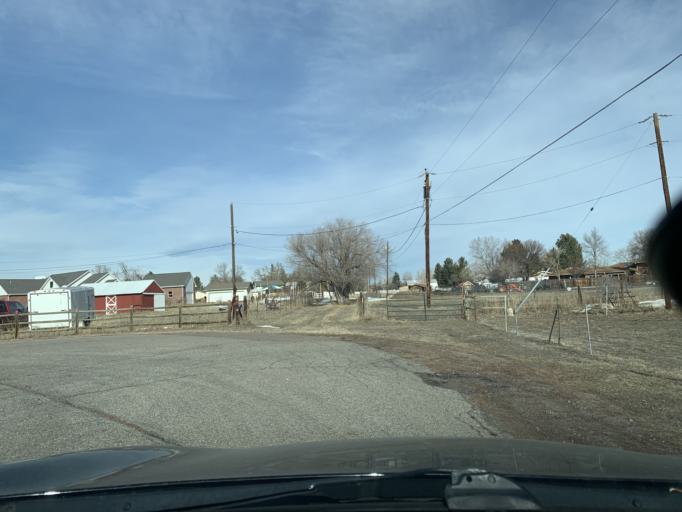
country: US
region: Colorado
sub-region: Jefferson County
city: Applewood
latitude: 39.7922
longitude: -105.1793
